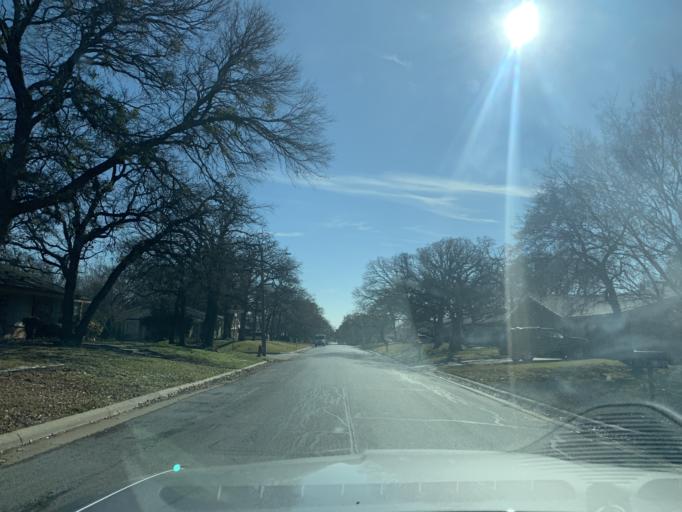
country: US
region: Texas
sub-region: Tarrant County
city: Bedford
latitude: 32.8472
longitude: -97.1510
